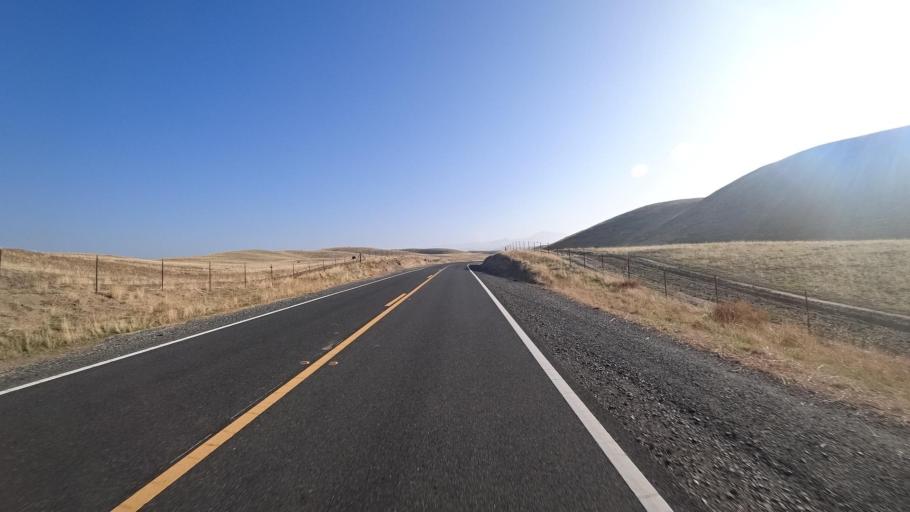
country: US
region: California
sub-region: Tulare County
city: Richgrove
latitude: 35.7434
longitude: -118.9457
